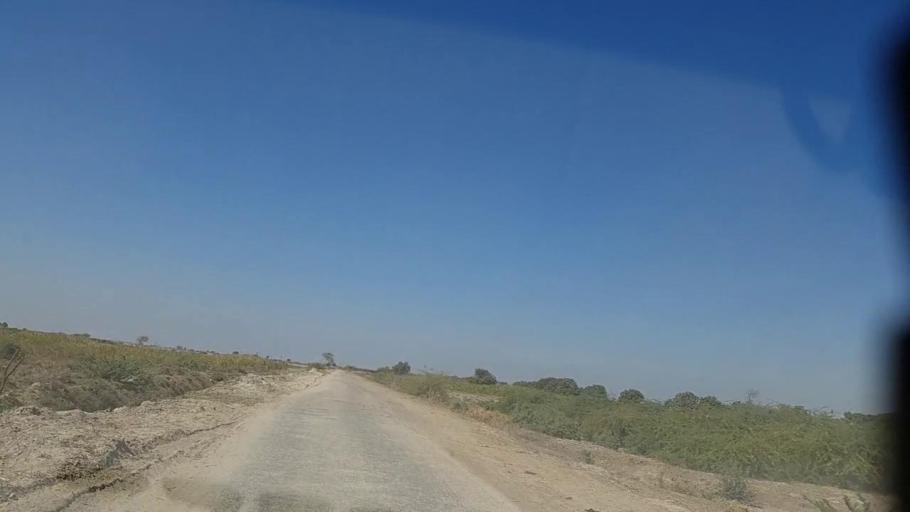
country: PK
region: Sindh
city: Mirwah Gorchani
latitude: 25.2237
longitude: 69.0220
